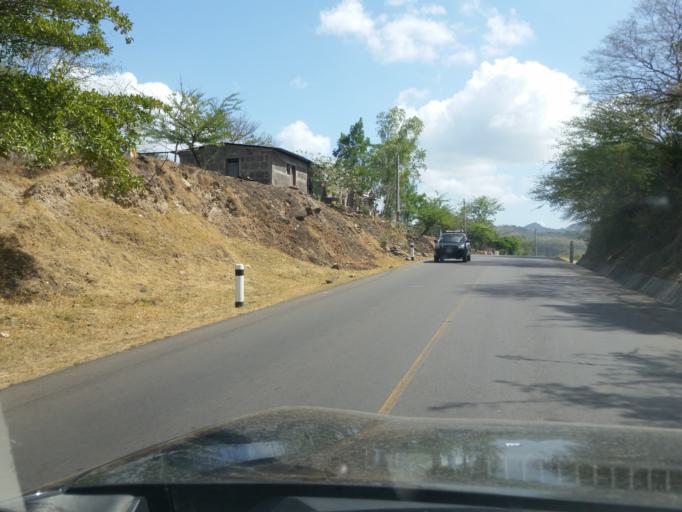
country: NI
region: Boaco
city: San Lorenzo
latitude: 12.2667
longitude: -85.6507
